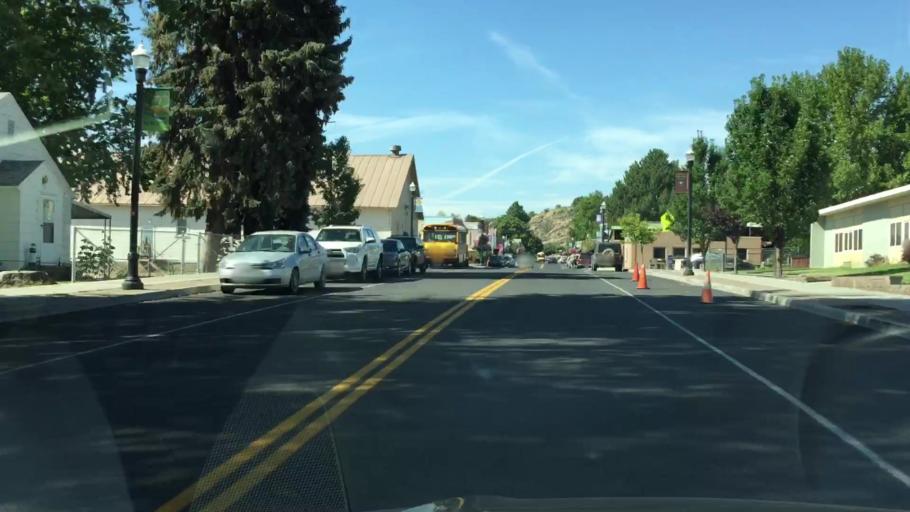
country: US
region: Oregon
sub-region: Wasco County
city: The Dalles
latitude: 45.1762
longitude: -121.0787
